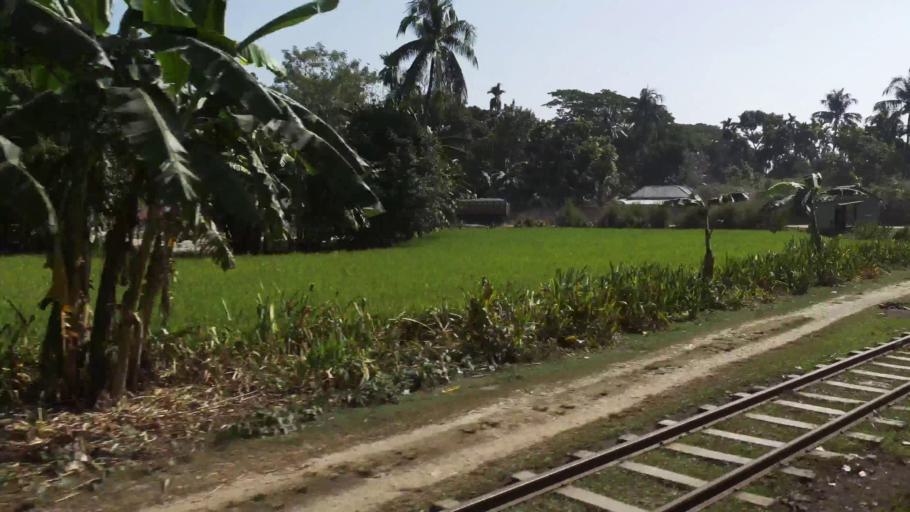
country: BD
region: Dhaka
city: Gafargaon
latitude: 24.5470
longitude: 90.5085
